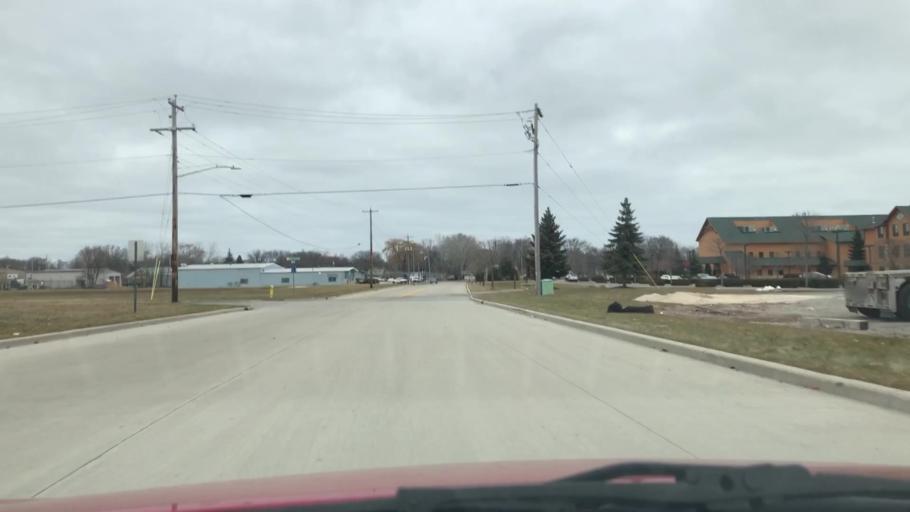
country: US
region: Wisconsin
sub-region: Brown County
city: Ashwaubenon
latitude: 44.4949
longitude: -88.0483
